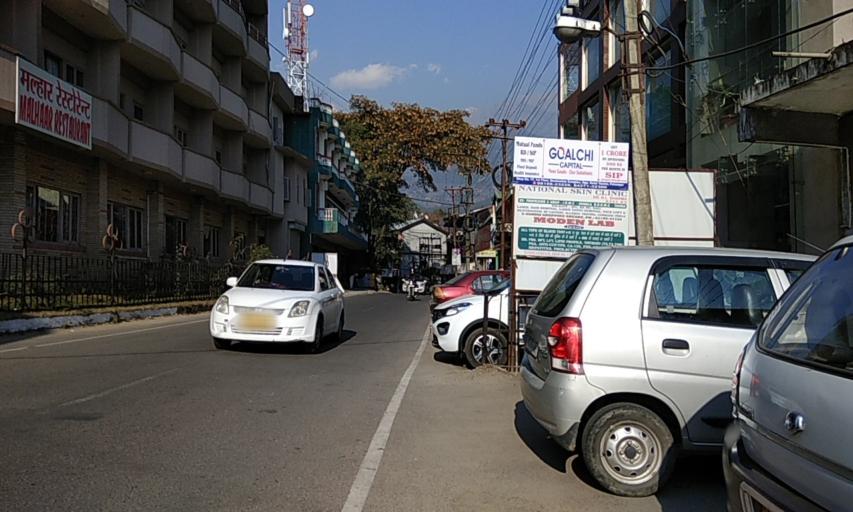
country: IN
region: Himachal Pradesh
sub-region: Kangra
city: Palampur
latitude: 32.1129
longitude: 76.5343
